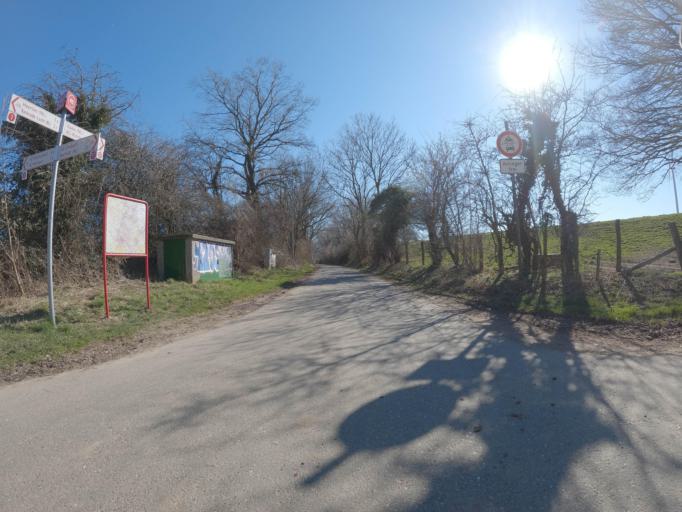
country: NL
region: Limburg
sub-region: Gemeente Kerkrade
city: Kerkrade
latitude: 50.8303
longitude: 6.0319
